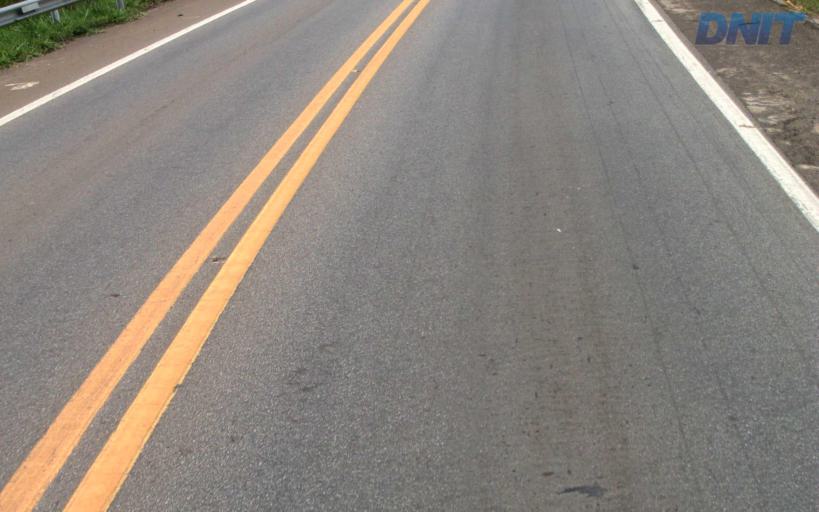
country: BR
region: Minas Gerais
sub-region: Ipaba
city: Ipaba
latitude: -19.3735
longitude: -42.4608
